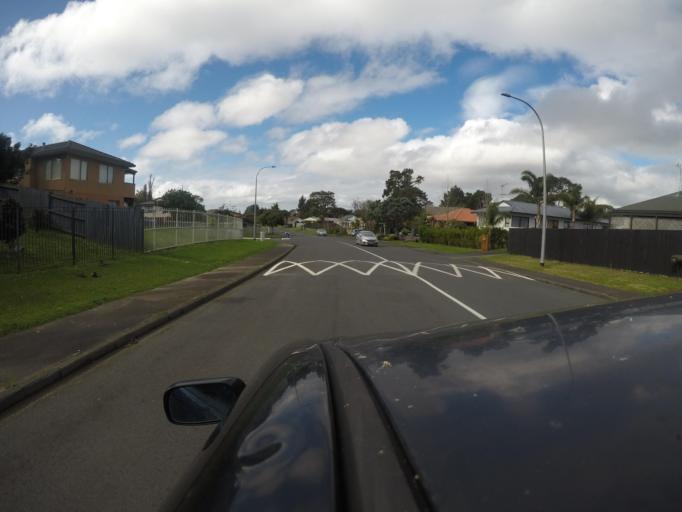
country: NZ
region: Auckland
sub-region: Auckland
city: Waitakere
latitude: -36.8960
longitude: 174.6565
